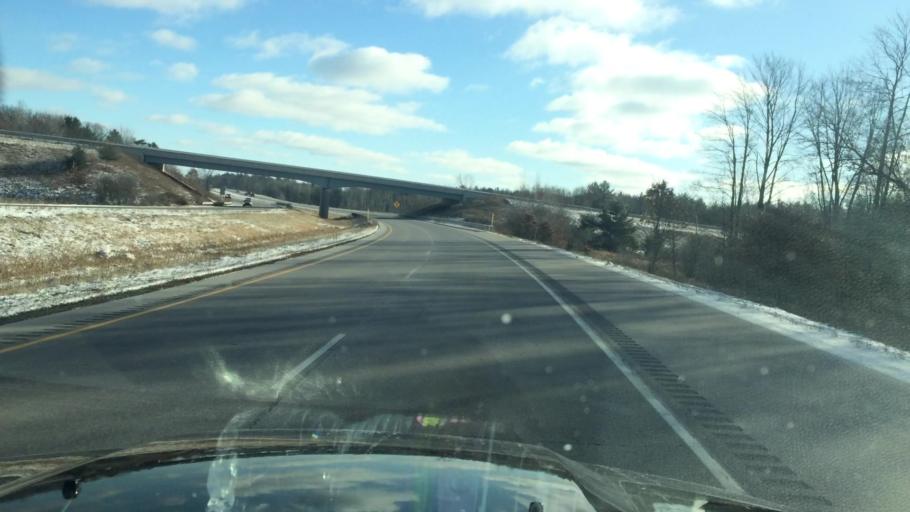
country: US
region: Wisconsin
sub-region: Portage County
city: Stevens Point
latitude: 44.5488
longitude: -89.5788
